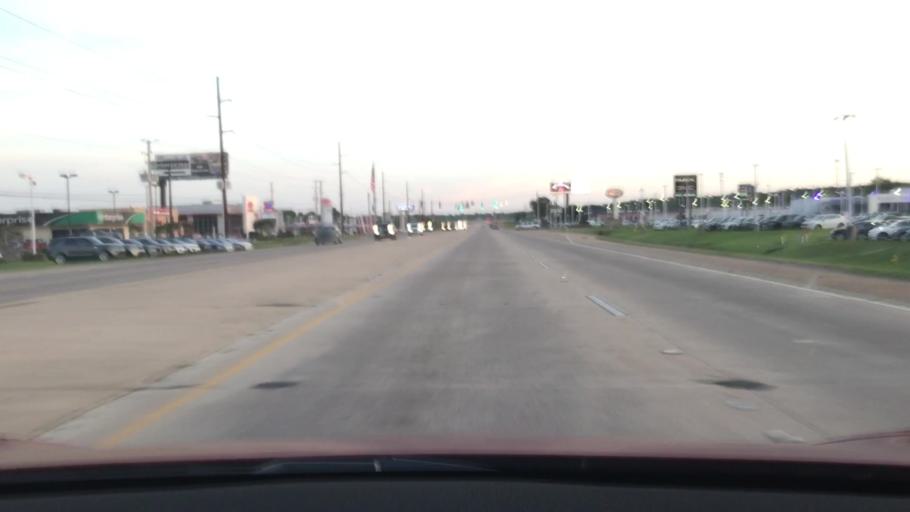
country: US
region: Louisiana
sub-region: Bossier Parish
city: Bossier City
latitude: 32.4216
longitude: -93.7209
